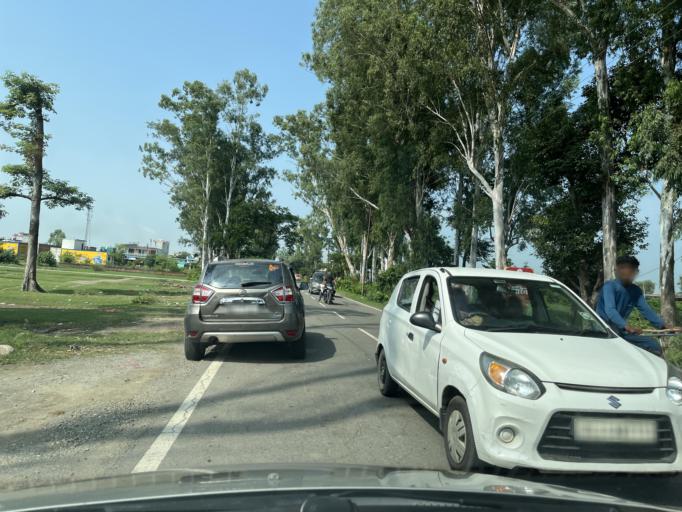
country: IN
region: Uttarakhand
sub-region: Udham Singh Nagar
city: Bazpur
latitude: 29.2120
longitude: 79.2189
